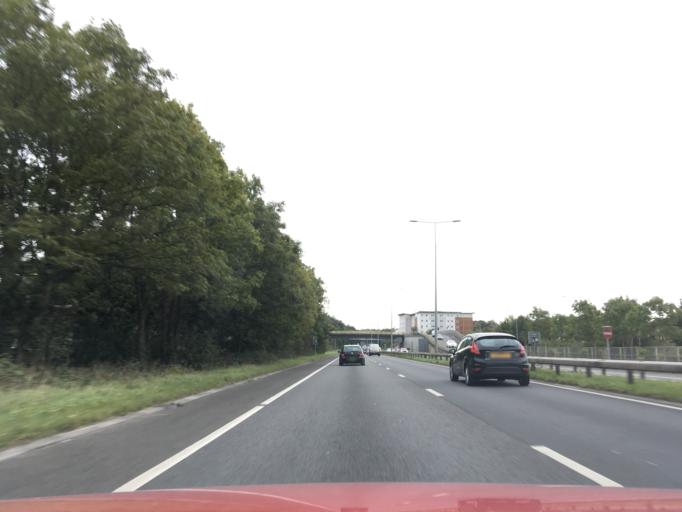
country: GB
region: Wales
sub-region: Cardiff
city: Cardiff
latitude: 51.5055
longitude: -3.1903
